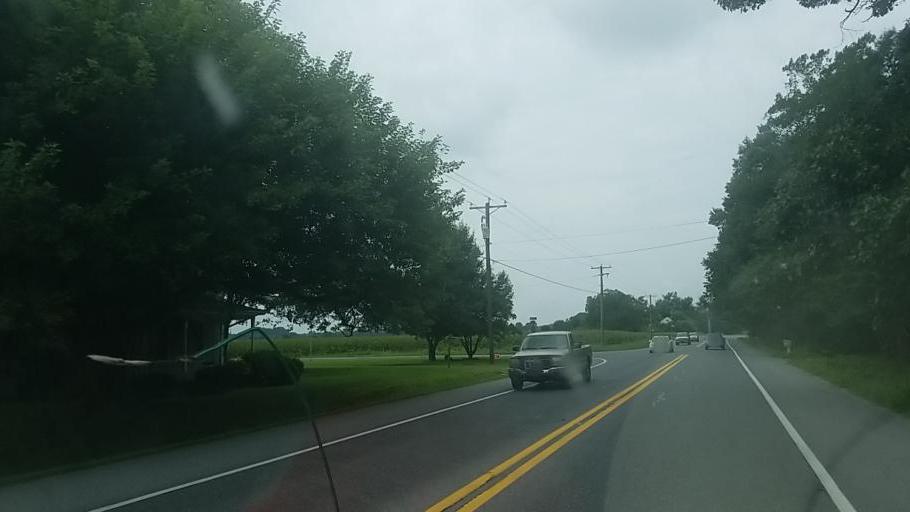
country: US
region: Delaware
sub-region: Sussex County
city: Long Neck
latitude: 38.5543
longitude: -75.1812
